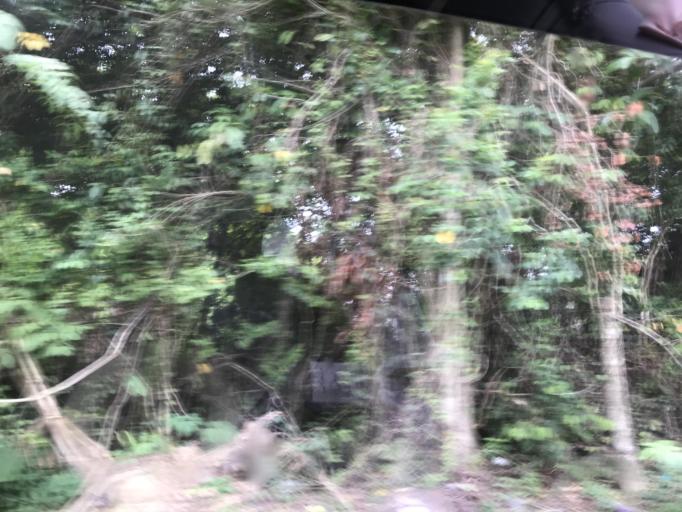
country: MY
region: Kelantan
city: Kota Bharu
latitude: 6.1185
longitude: 102.2061
